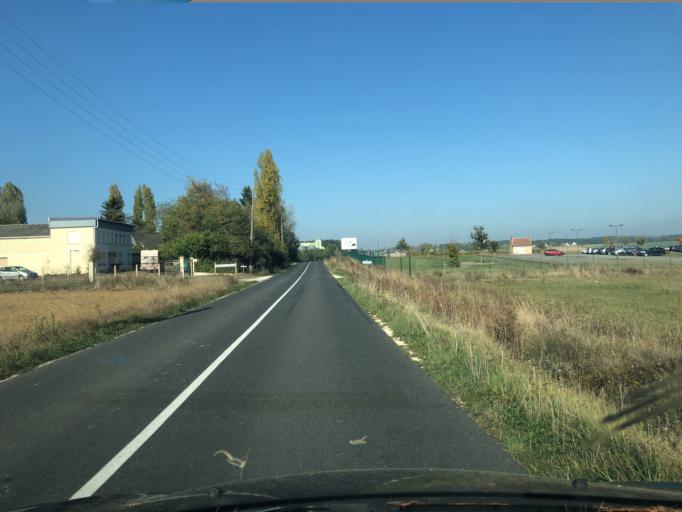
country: FR
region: Centre
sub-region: Departement d'Indre-et-Loire
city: Rouziers-de-Touraine
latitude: 47.5016
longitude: 0.6522
